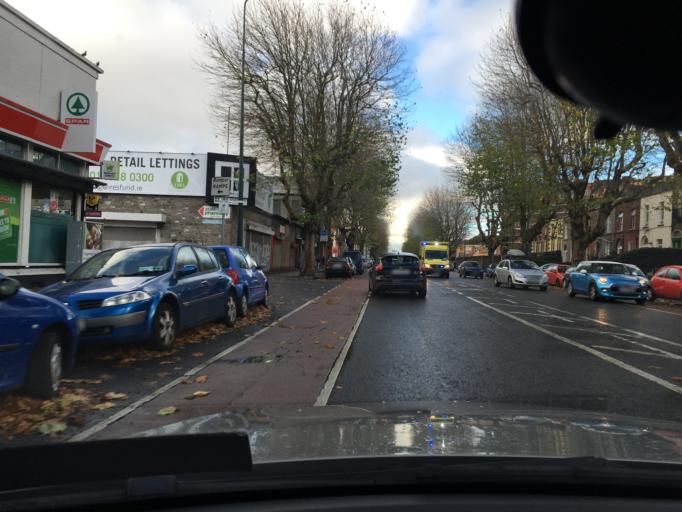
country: IE
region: Leinster
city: Drumcondra
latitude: 53.3589
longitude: -6.2571
